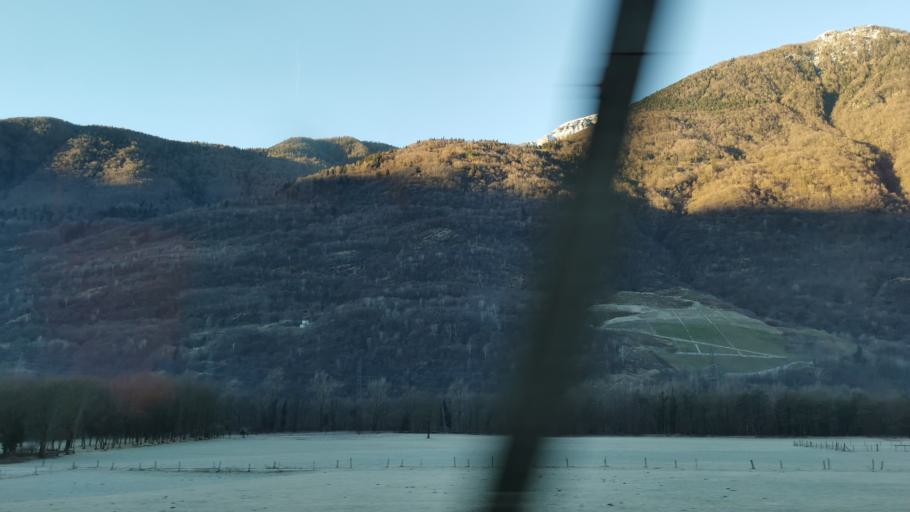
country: CH
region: Ticino
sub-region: Riviera District
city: Claro
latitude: 46.2480
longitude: 9.0192
